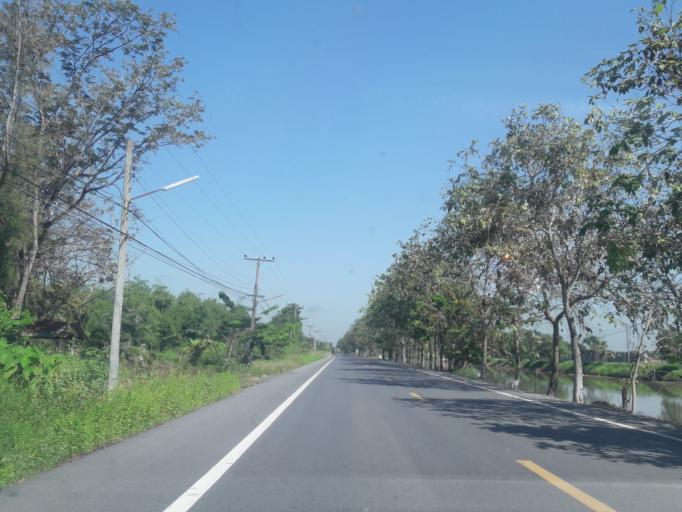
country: TH
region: Pathum Thani
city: Nong Suea
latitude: 14.1577
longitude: 100.8459
